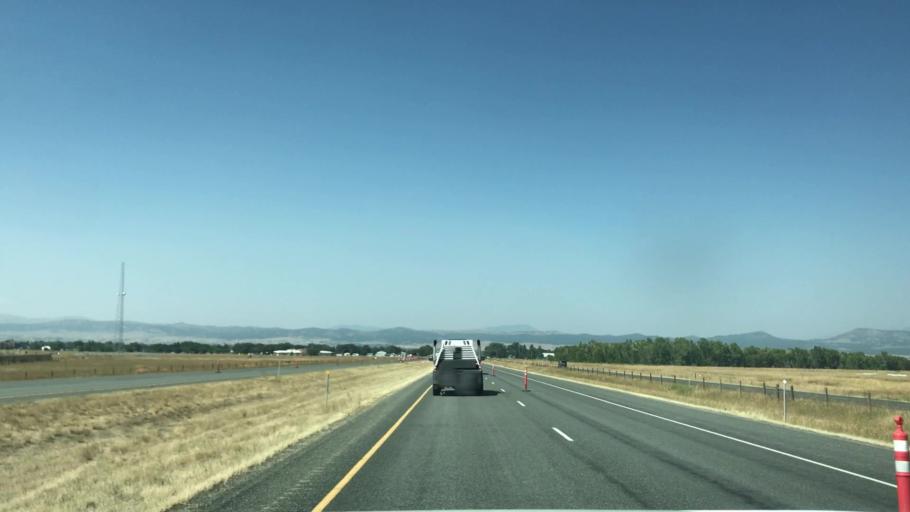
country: US
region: Montana
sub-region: Lewis and Clark County
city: Helena Valley West Central
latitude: 46.6497
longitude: -112.0112
